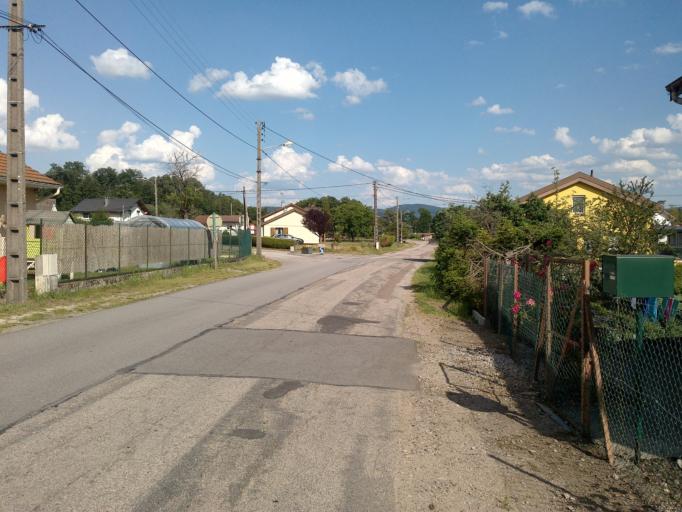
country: FR
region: Lorraine
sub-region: Departement des Vosges
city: Archettes
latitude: 48.1232
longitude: 6.5370
